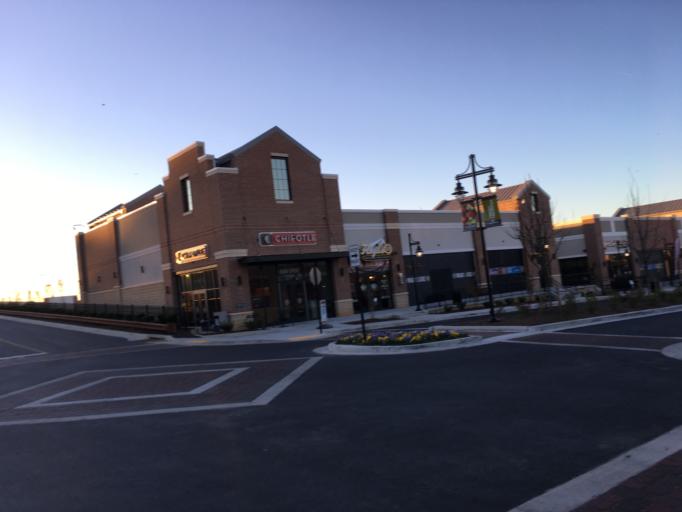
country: US
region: Maryland
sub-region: Baltimore County
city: Owings Mills
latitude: 39.4131
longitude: -76.7724
